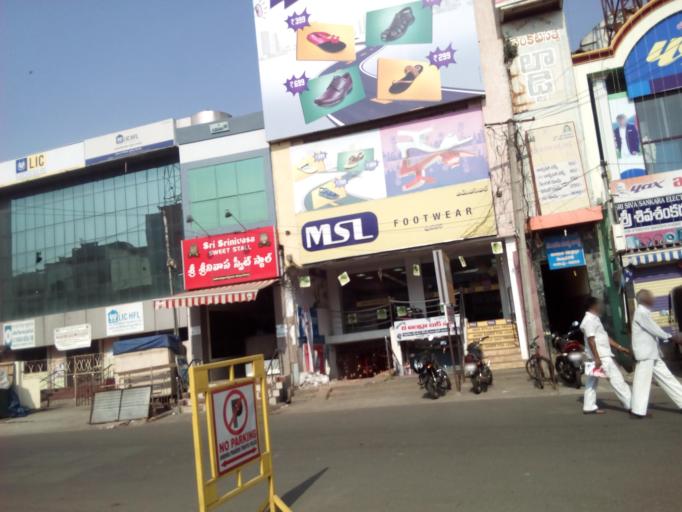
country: IN
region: Andhra Pradesh
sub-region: East Godavari
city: Rajahmundry
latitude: 16.9964
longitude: 81.7737
